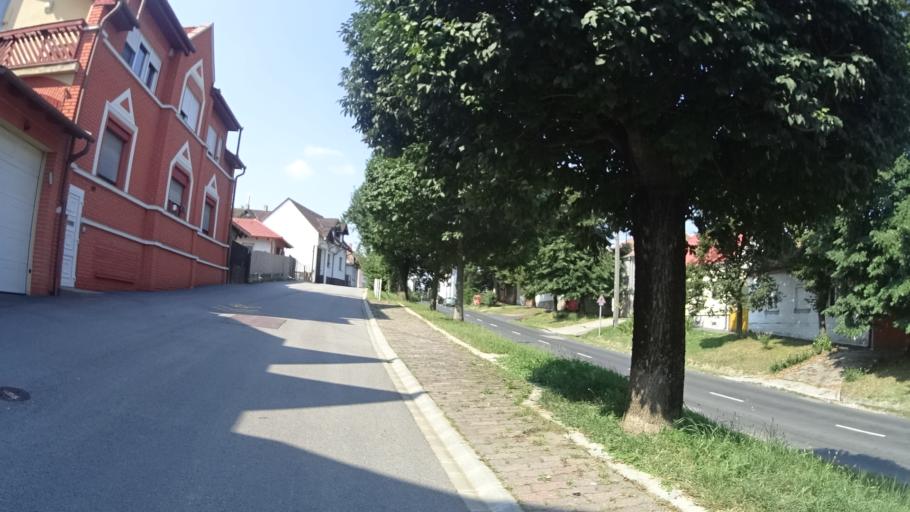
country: HU
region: Zala
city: Nagykanizsa
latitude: 46.4607
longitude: 16.9987
